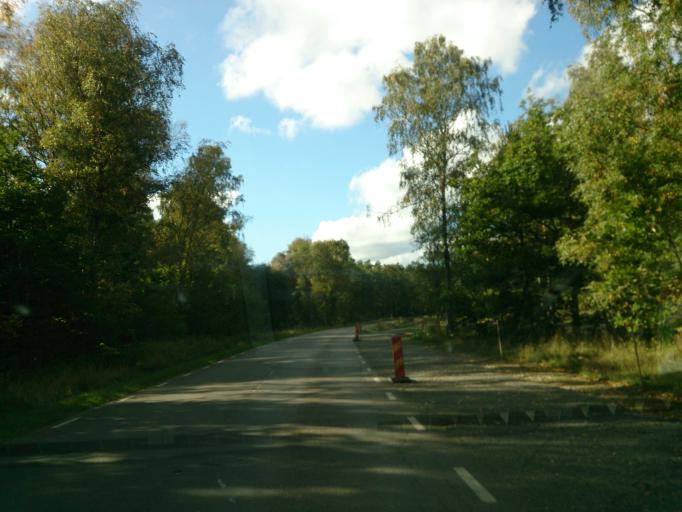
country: SE
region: Skane
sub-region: Sjobo Kommun
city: Blentarp
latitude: 55.5894
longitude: 13.6549
